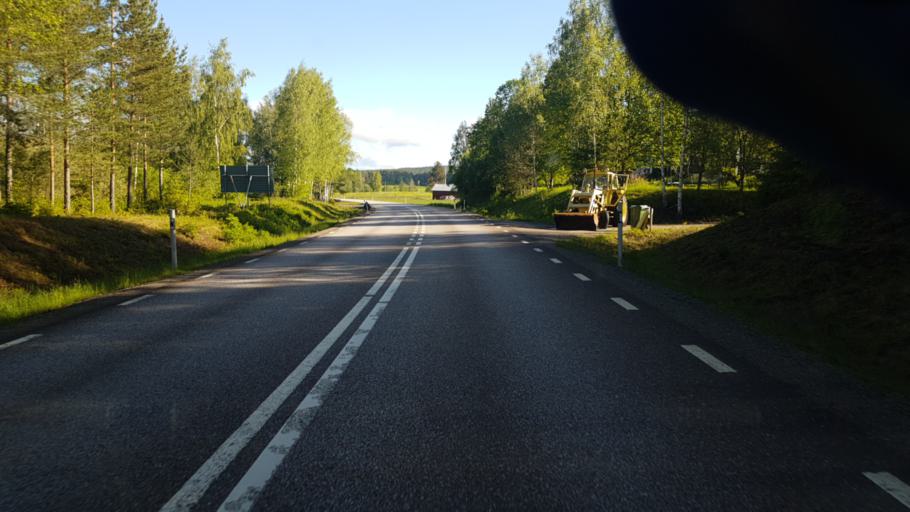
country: SE
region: Vaermland
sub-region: Arvika Kommun
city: Arvika
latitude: 59.4620
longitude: 12.7742
